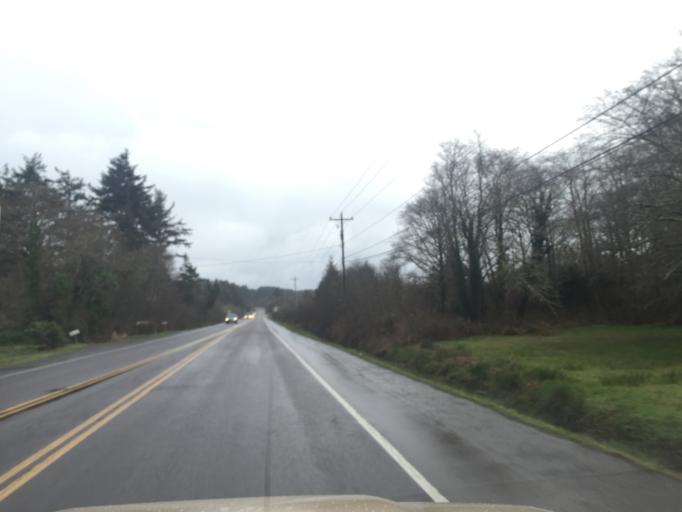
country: US
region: Oregon
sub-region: Lincoln County
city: Newport
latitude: 44.5987
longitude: -124.0592
